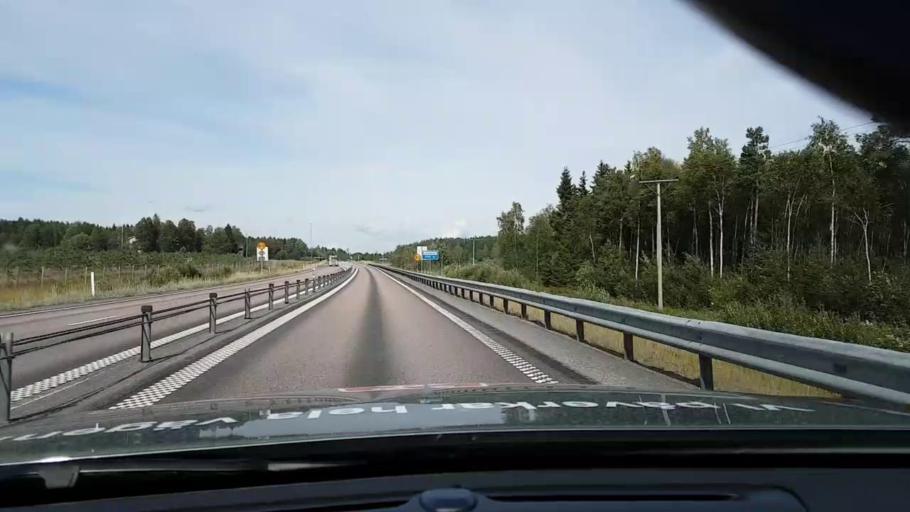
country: SE
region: Vaesternorrland
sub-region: OErnskoeldsviks Kommun
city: Husum
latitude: 63.4131
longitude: 19.2060
